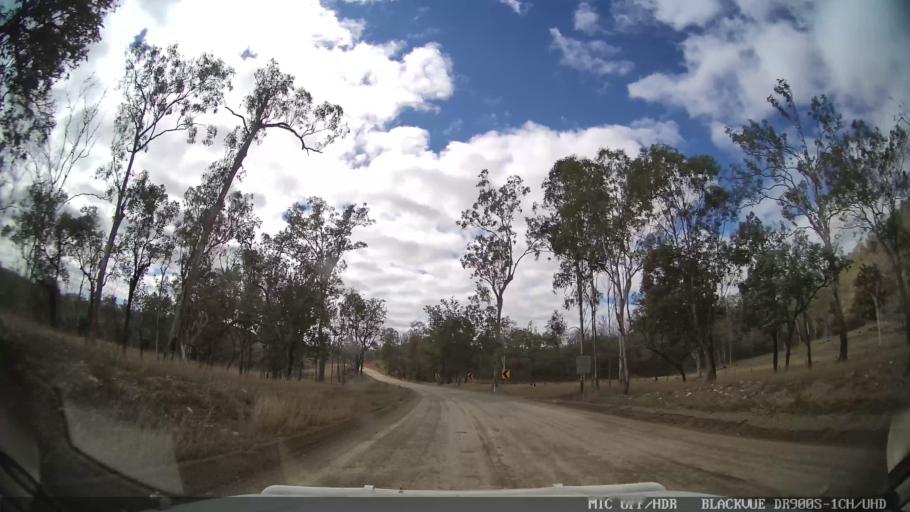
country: AU
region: Queensland
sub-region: Gladstone
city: Toolooa
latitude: -24.6199
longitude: 151.2967
